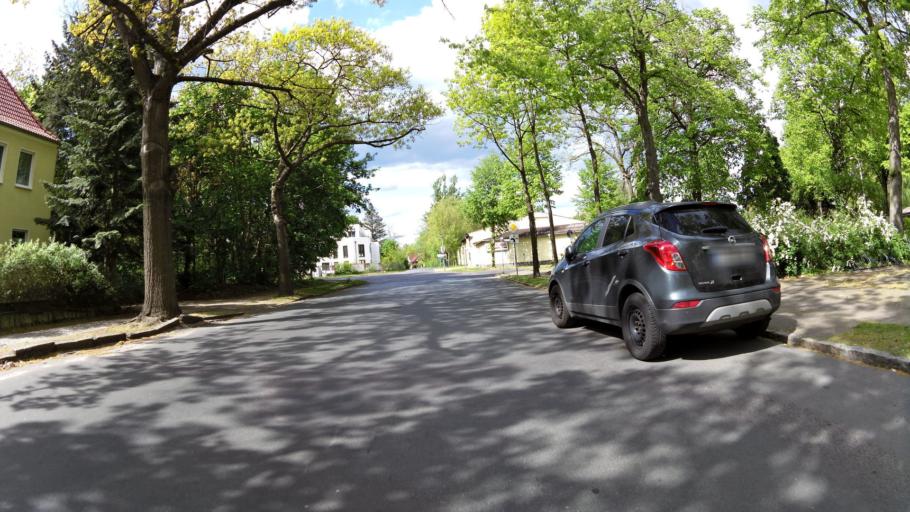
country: DE
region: Brandenburg
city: Furstenwalde
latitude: 52.3557
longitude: 14.0544
